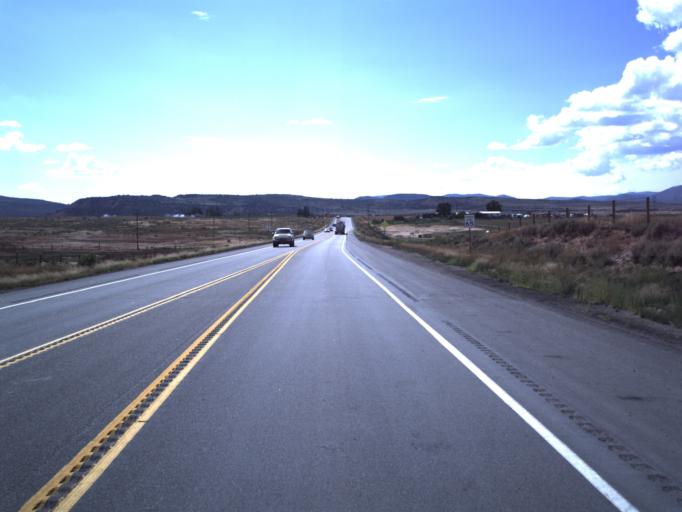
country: US
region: Utah
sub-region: Duchesne County
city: Duchesne
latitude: 40.2124
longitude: -110.8418
